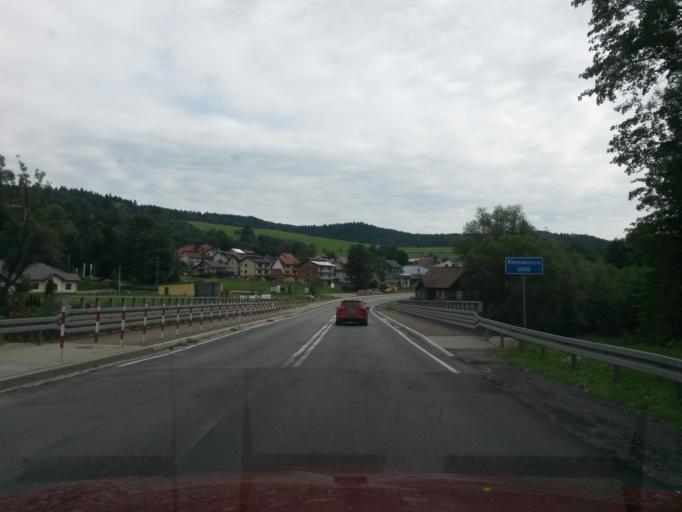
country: PL
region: Lesser Poland Voivodeship
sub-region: Powiat nowosadecki
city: Labowa
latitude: 49.4965
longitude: 20.9056
